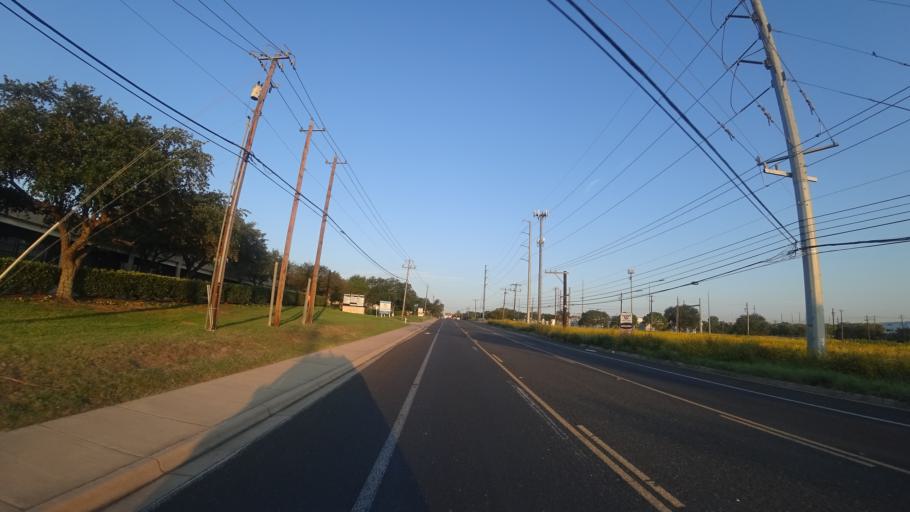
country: US
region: Texas
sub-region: Travis County
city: Austin
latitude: 30.3383
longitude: -97.6855
